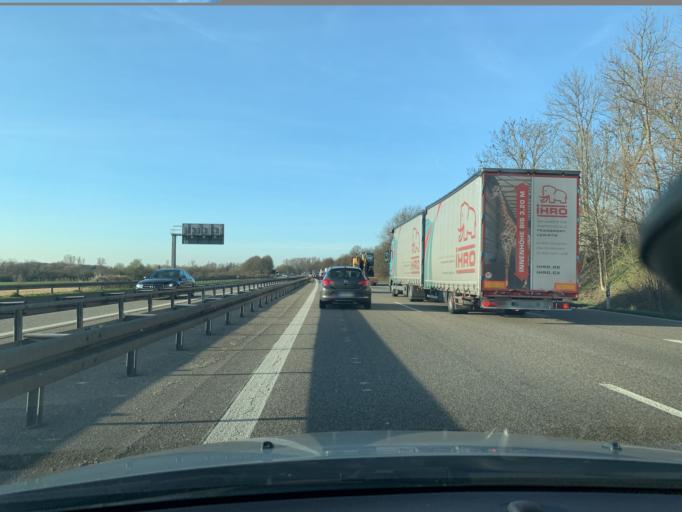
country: DE
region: Baden-Wuerttemberg
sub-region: Freiburg Region
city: Vorstetten
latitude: 48.0647
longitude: 7.8122
